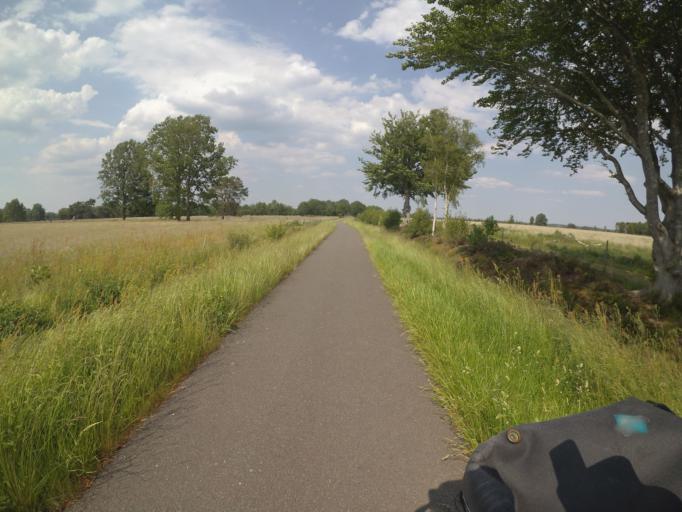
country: NL
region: Drenthe
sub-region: Gemeente Assen
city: Assen
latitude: 52.9617
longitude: 6.4969
